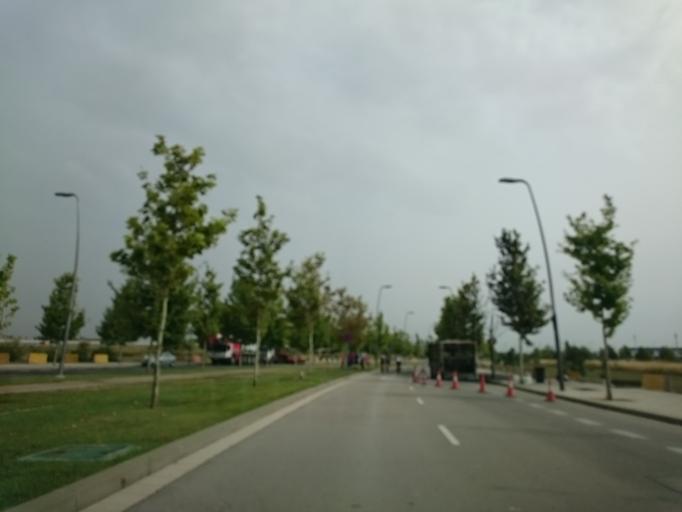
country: ES
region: Catalonia
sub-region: Provincia de Barcelona
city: Viladecans
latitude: 41.2966
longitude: 2.0525
